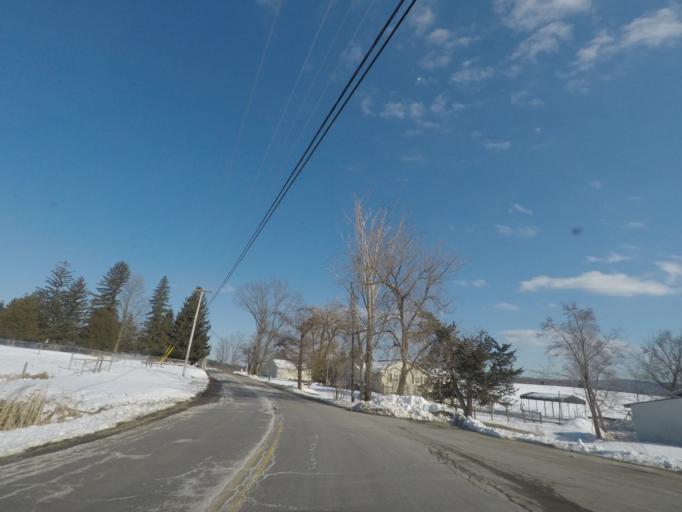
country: US
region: New York
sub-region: Rensselaer County
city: Hoosick Falls
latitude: 42.8535
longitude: -73.4993
